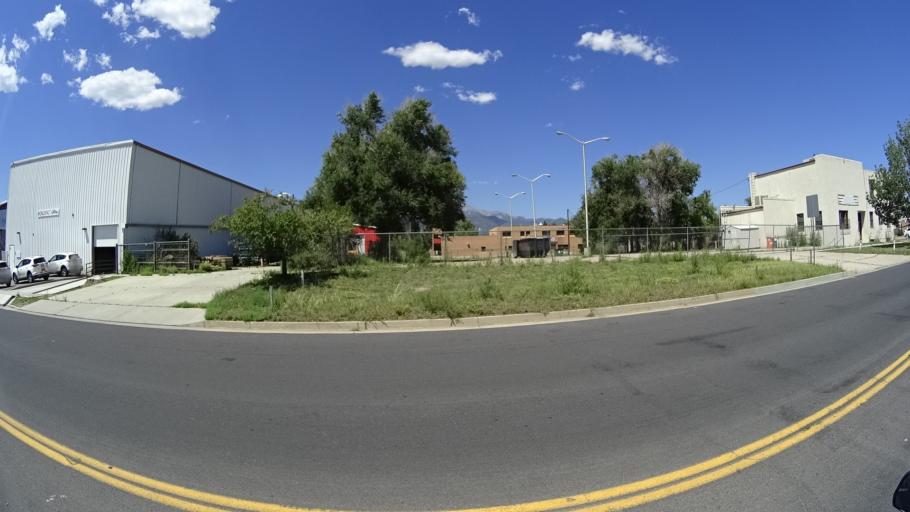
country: US
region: Colorado
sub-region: El Paso County
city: Colorado Springs
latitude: 38.8262
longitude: -104.8184
